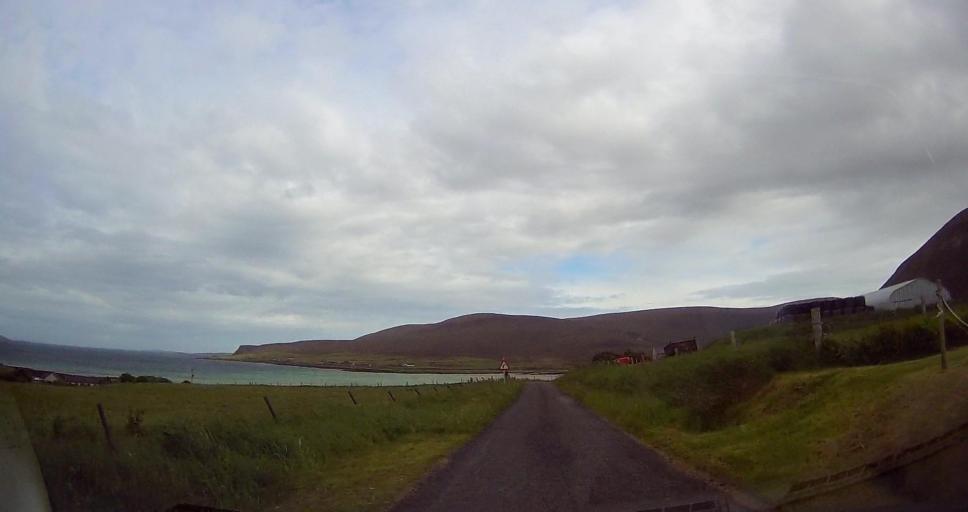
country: GB
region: Scotland
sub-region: Orkney Islands
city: Stromness
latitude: 58.9127
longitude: -3.3221
